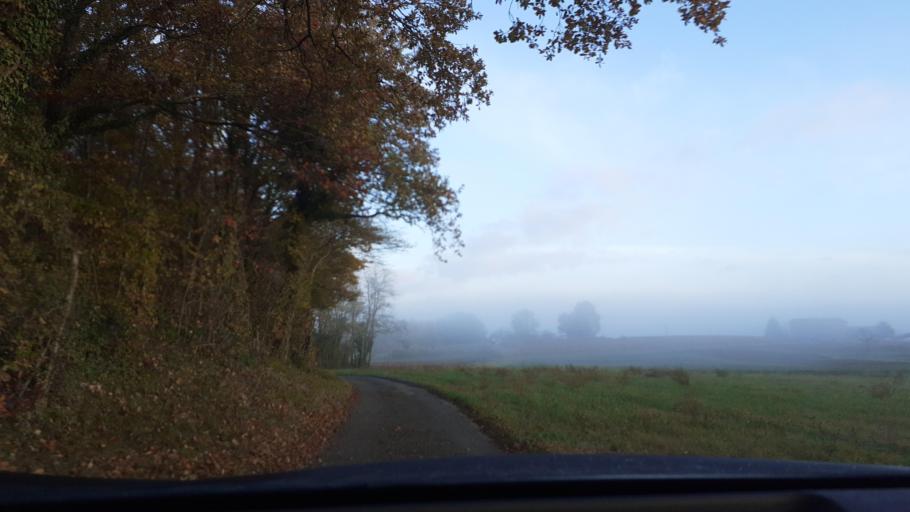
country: FR
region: Rhone-Alpes
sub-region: Departement du Rhone
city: Charnay
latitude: 45.9111
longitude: 4.6686
